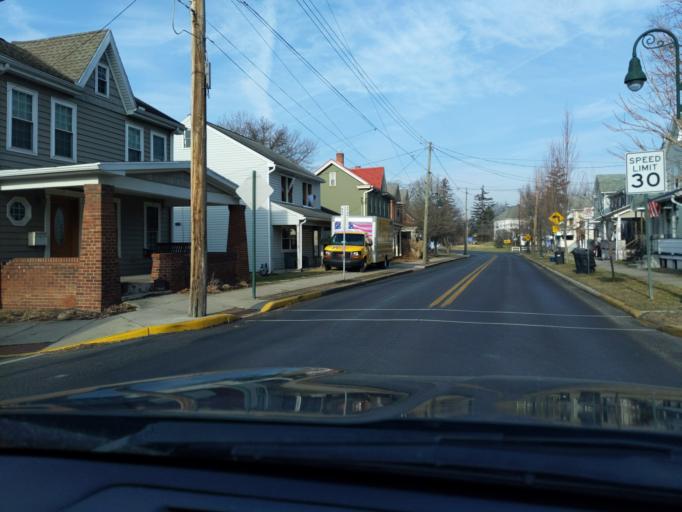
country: US
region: Pennsylvania
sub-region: Blair County
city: Hollidaysburg
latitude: 40.4314
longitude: -78.3994
